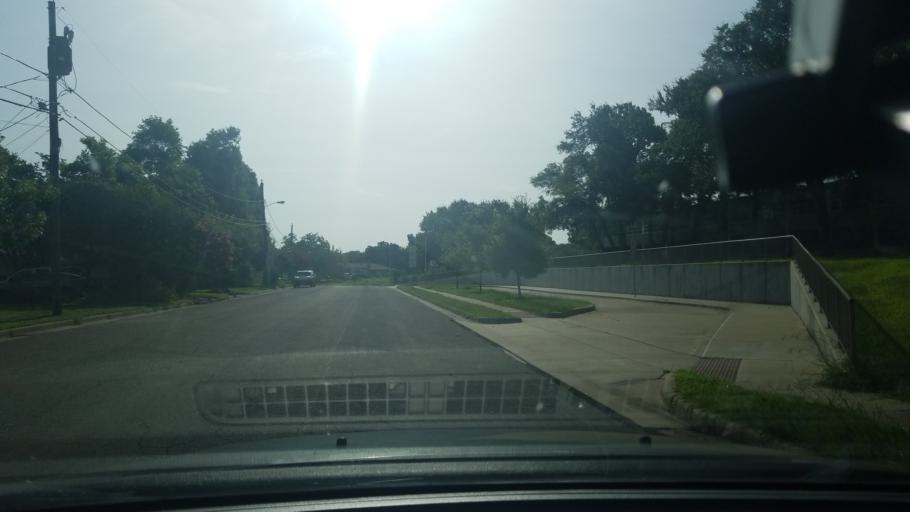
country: US
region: Texas
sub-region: Dallas County
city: Highland Park
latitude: 32.8015
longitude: -96.7077
